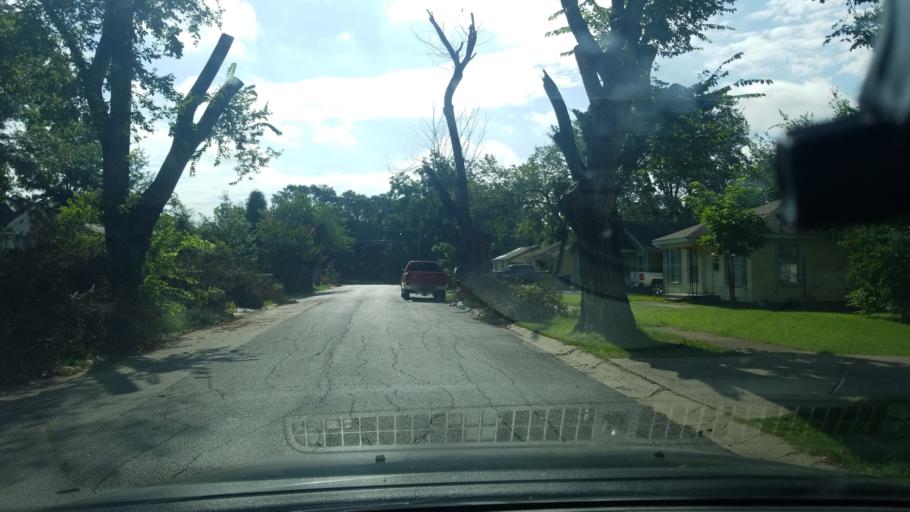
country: US
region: Texas
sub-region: Dallas County
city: Balch Springs
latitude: 32.7331
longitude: -96.6754
